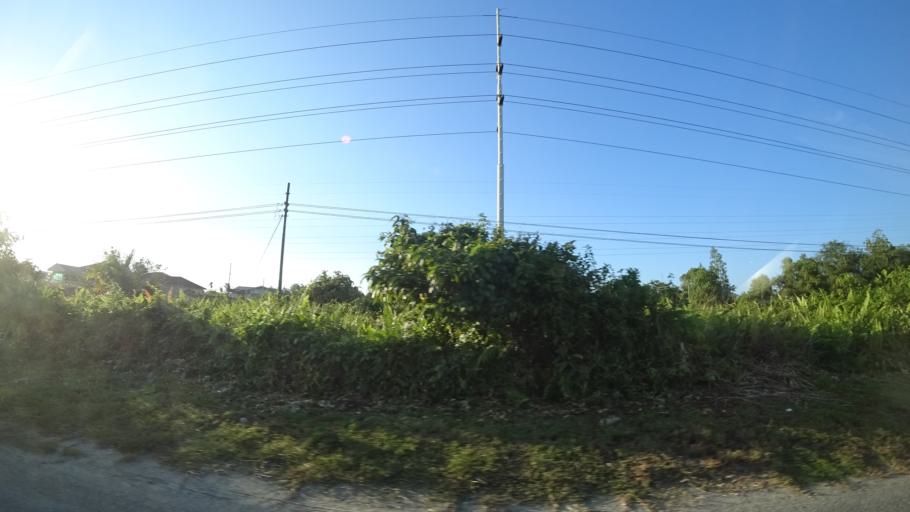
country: BN
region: Tutong
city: Tutong
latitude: 4.7275
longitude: 114.5525
